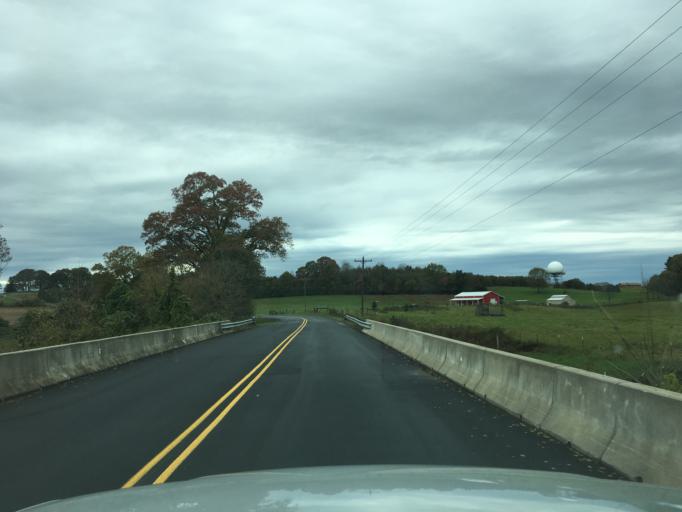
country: US
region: North Carolina
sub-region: Catawba County
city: Maiden
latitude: 35.6086
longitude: -81.2303
